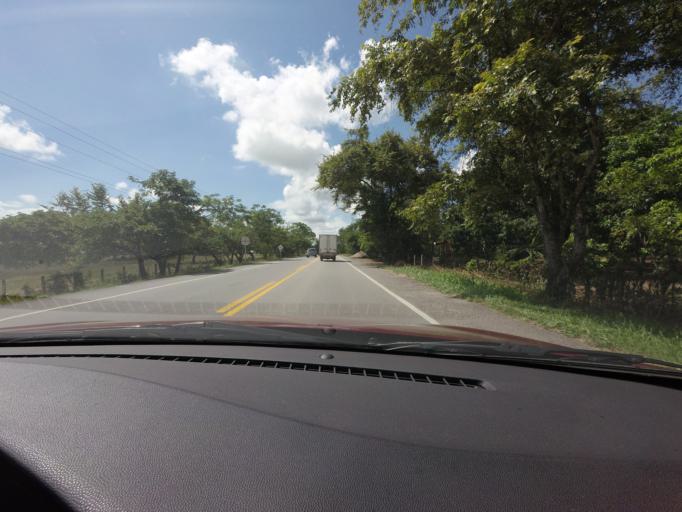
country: CO
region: Tolima
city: Saldana
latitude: 3.9479
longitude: -75.0088
